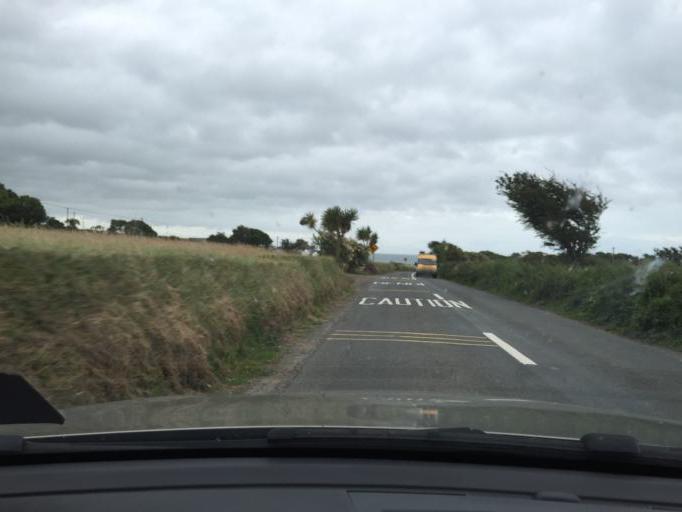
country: IE
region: Munster
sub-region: County Cork
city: Youghal
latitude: 51.9638
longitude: -7.7179
